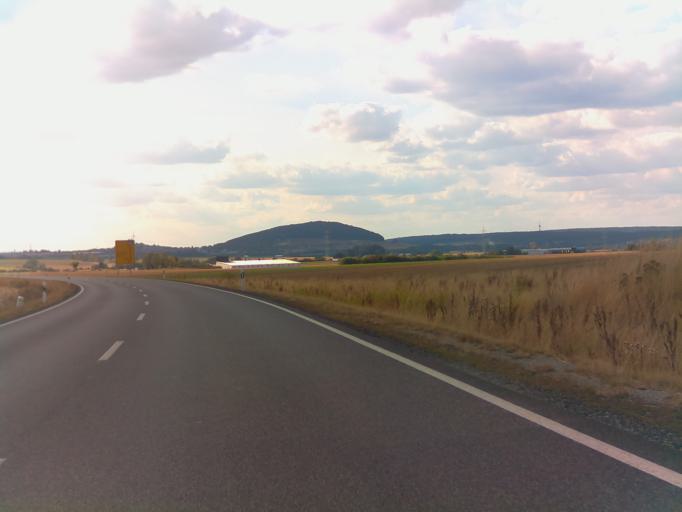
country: DE
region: Hesse
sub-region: Regierungsbezirk Kassel
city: Dipperz
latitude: 50.5440
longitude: 9.7803
